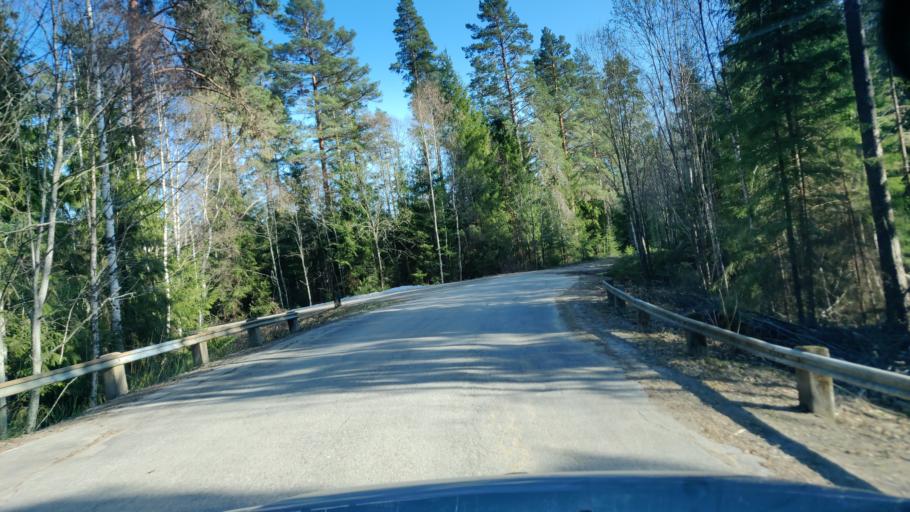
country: SE
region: Vaermland
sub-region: Hagfors Kommun
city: Hagfors
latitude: 59.9726
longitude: 13.5526
